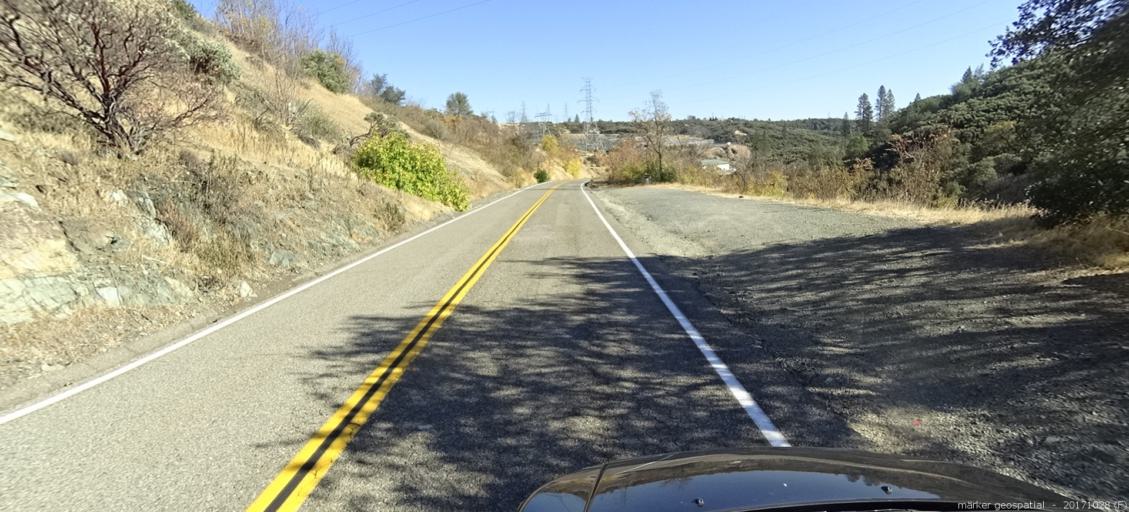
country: US
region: California
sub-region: Shasta County
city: Shasta
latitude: 40.6107
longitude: -122.4514
